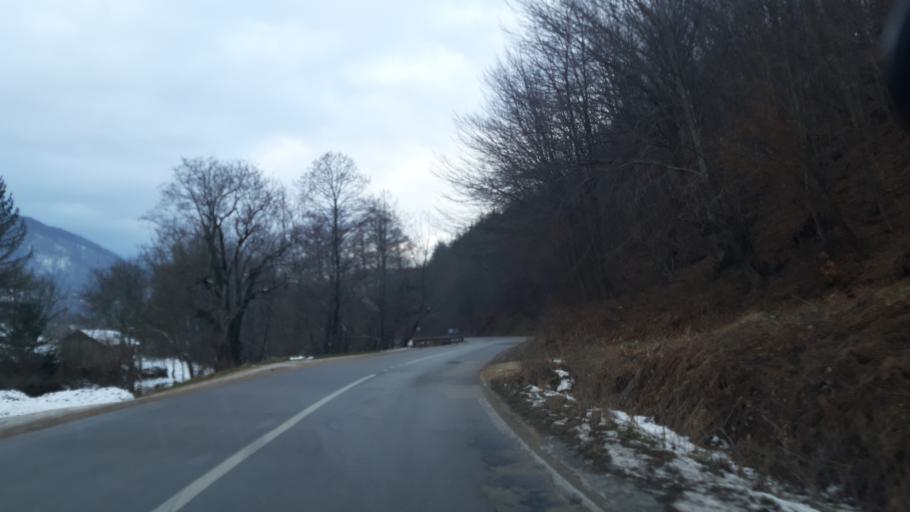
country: BA
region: Republika Srpska
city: Milici
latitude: 44.1686
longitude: 19.0311
